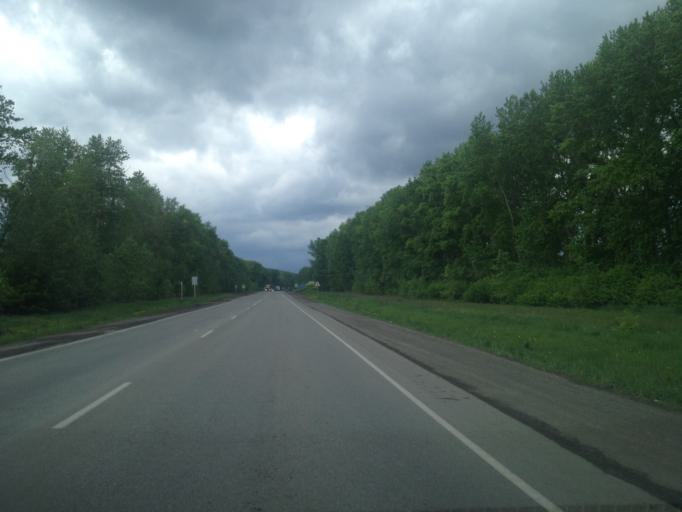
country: RU
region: Sverdlovsk
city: Aramil
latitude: 56.6951
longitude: 60.7838
